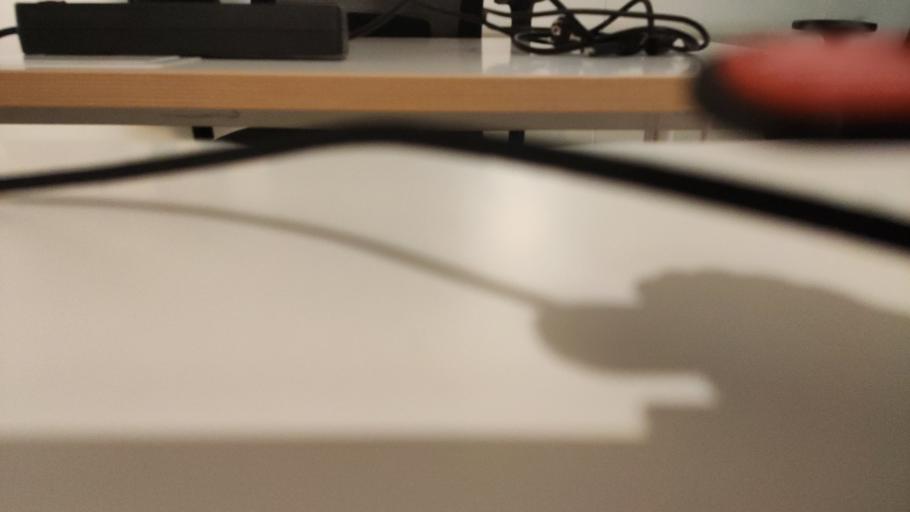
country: RU
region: Moskovskaya
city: Obolensk
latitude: 54.9881
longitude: 37.3059
